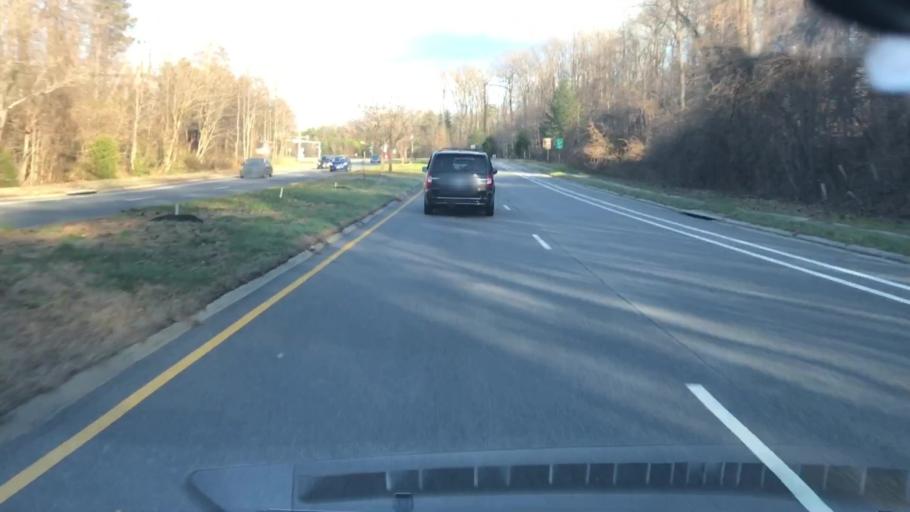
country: US
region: Virginia
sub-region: Fairfax County
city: Newington
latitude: 38.7387
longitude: -77.1663
